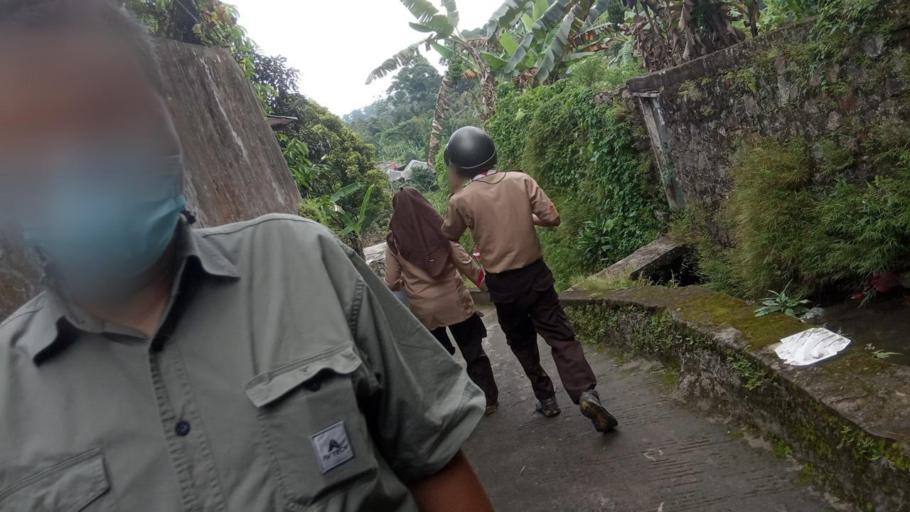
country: ID
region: West Java
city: Caringin
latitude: -6.6492
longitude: 106.8930
